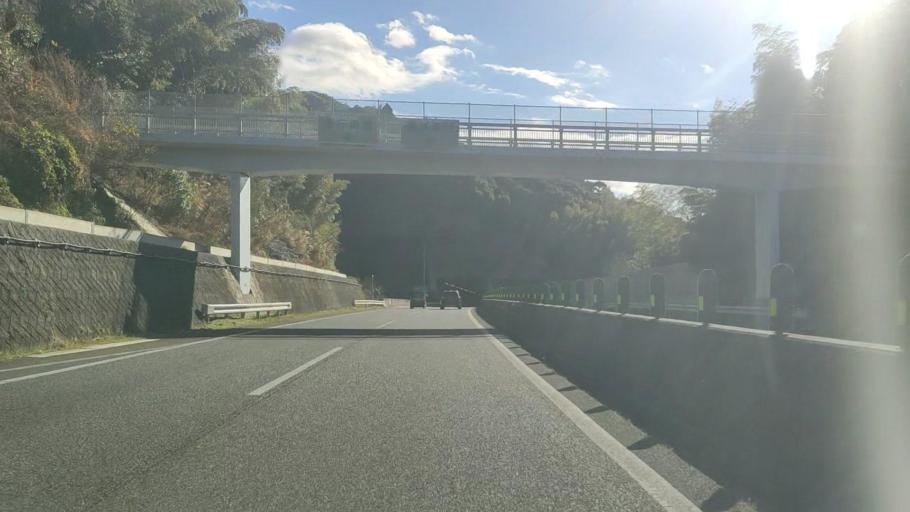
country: JP
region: Fukuoka
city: Kitakyushu
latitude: 33.8335
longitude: 130.7658
